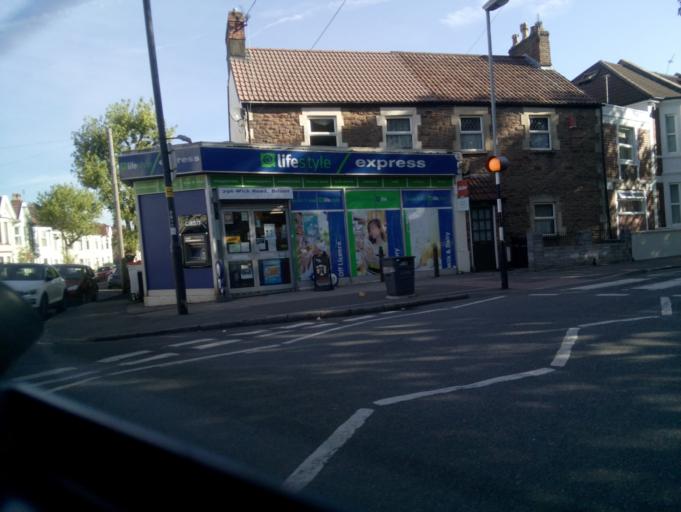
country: GB
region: England
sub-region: South Gloucestershire
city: Kingswood
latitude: 51.4455
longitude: -2.5486
